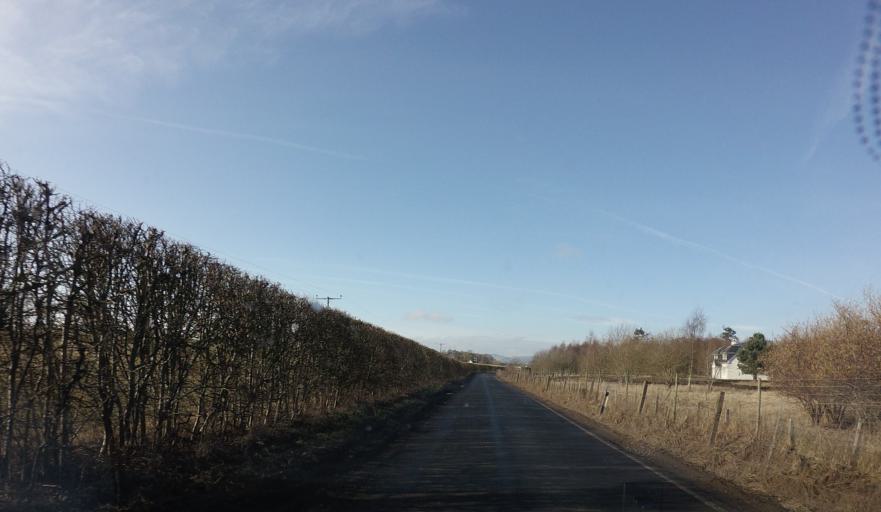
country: GB
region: Scotland
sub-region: Perth and Kinross
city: Stanley
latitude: 56.5251
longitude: -3.4451
